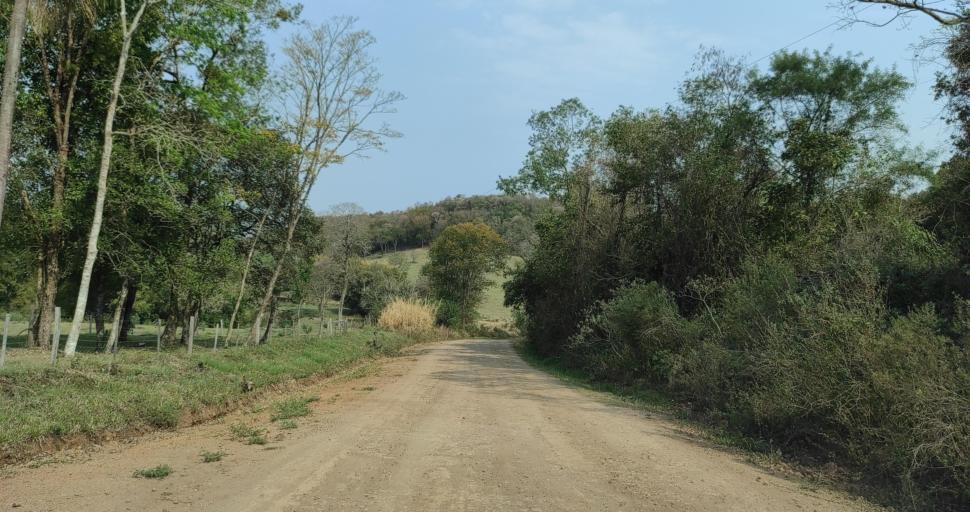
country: AR
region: Misiones
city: Cerro Cora
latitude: -27.5486
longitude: -55.5825
